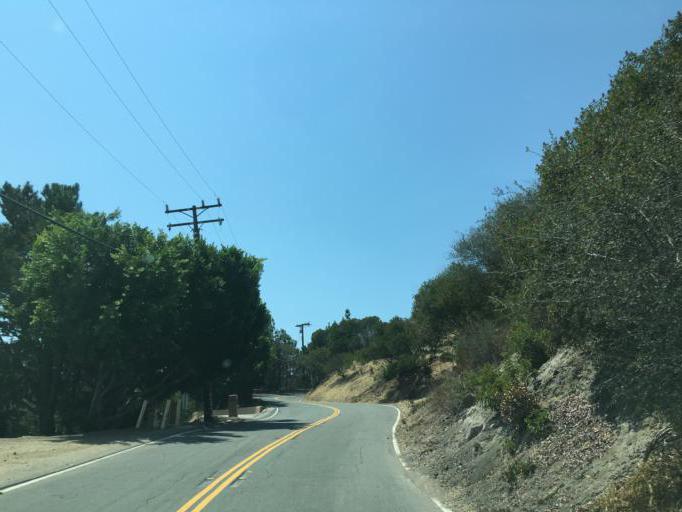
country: US
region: California
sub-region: Los Angeles County
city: Topanga
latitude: 34.0742
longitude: -118.6192
